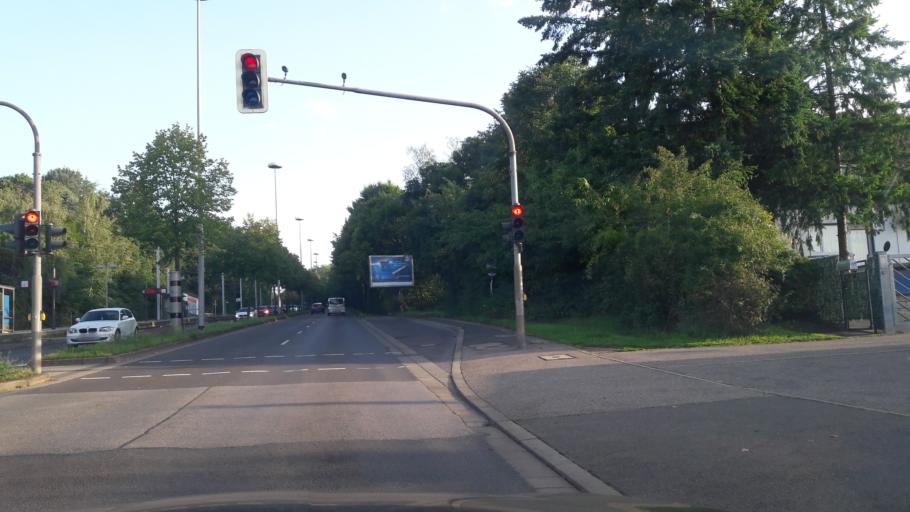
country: DE
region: Saarland
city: Saarbrucken
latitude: 49.2554
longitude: 6.9608
